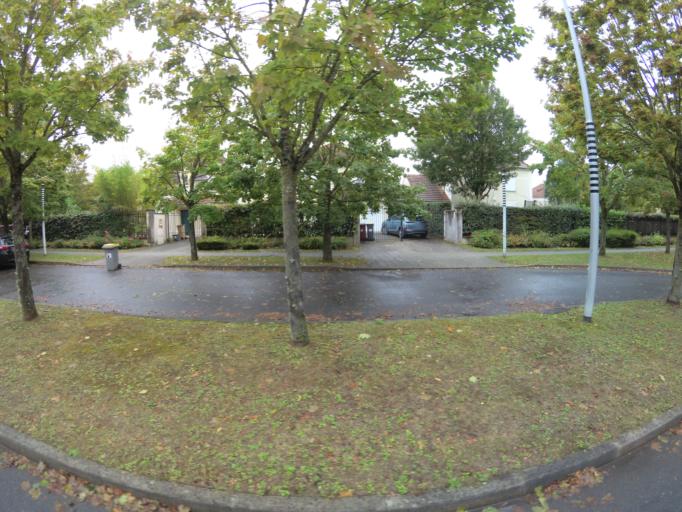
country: FR
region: Ile-de-France
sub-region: Departement de Seine-et-Marne
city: Chanteloup-en-Brie
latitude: 48.8448
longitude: 2.7315
